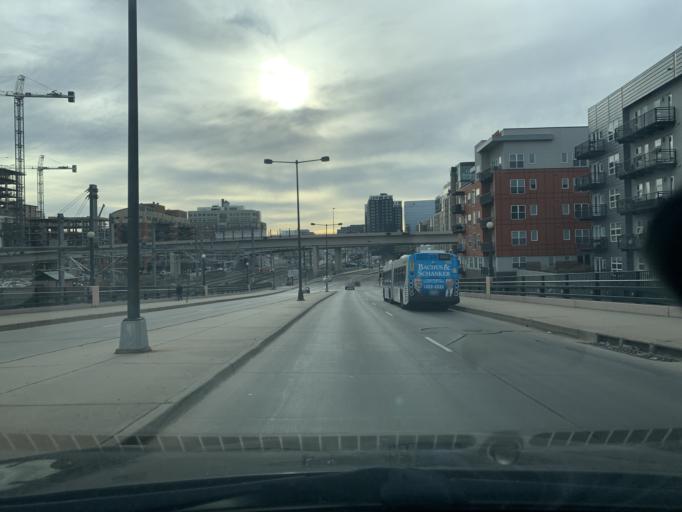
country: US
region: Colorado
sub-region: Denver County
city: Denver
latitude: 39.7578
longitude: -104.9956
